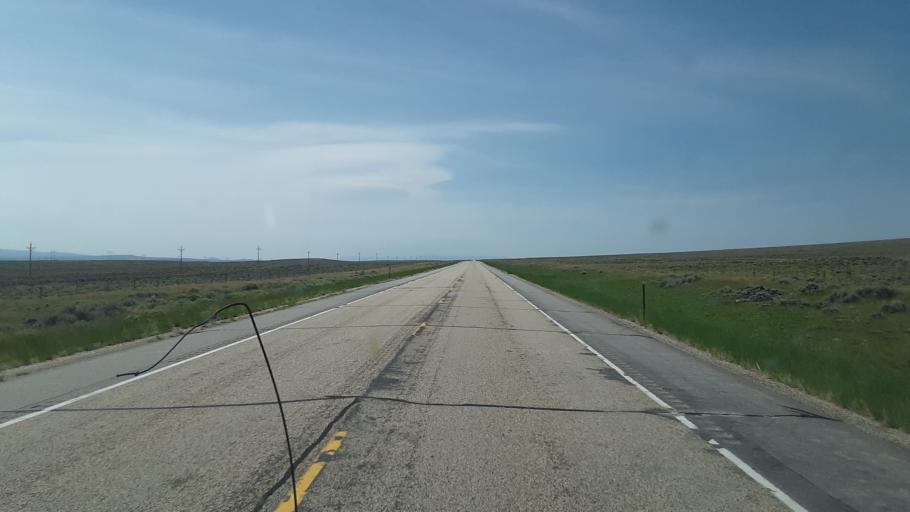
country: US
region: Wyoming
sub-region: Carbon County
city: Saratoga
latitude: 41.5896
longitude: -106.8158
